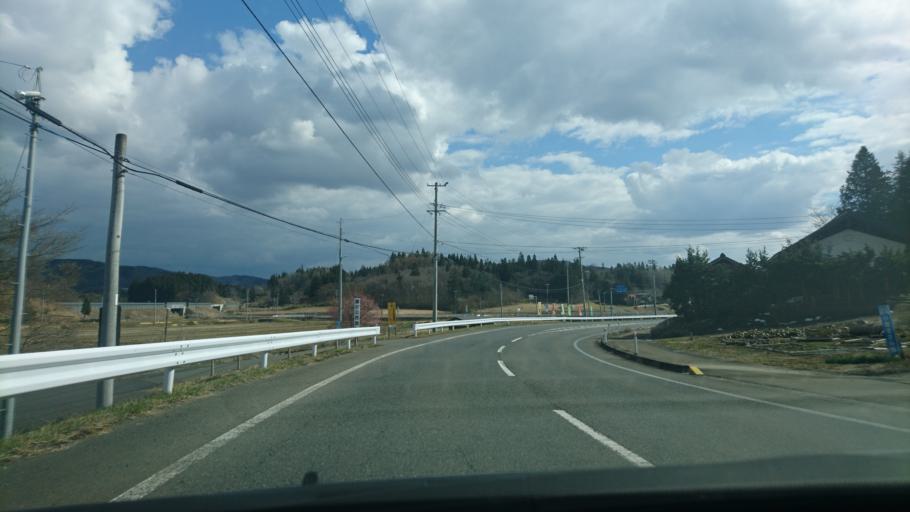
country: JP
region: Iwate
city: Hanamaki
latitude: 39.3469
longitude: 141.2397
